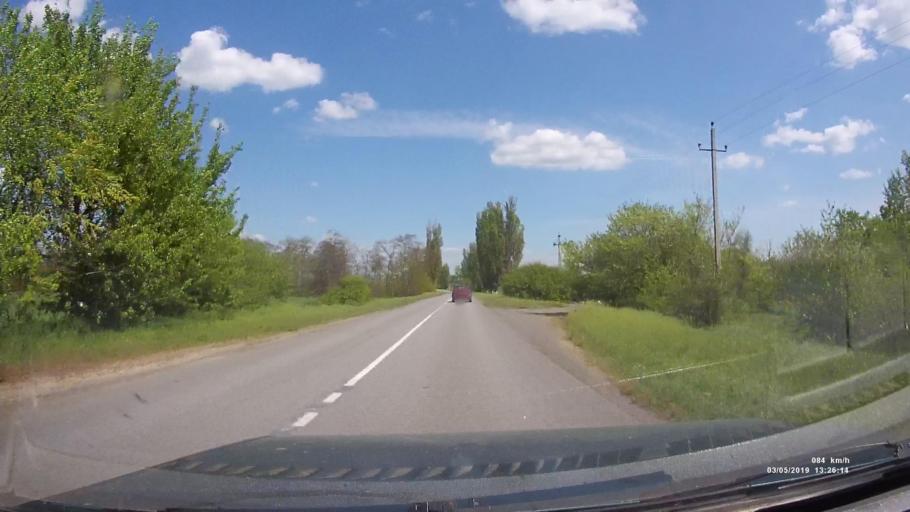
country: RU
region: Rostov
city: Semikarakorsk
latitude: 47.5708
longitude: 40.8163
